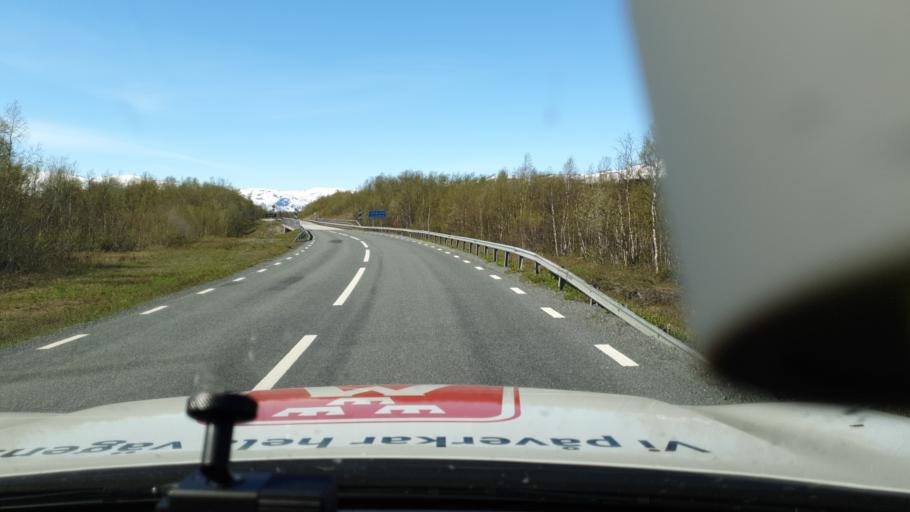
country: NO
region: Nordland
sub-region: Rana
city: Mo i Rana
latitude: 65.7804
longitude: 15.1130
